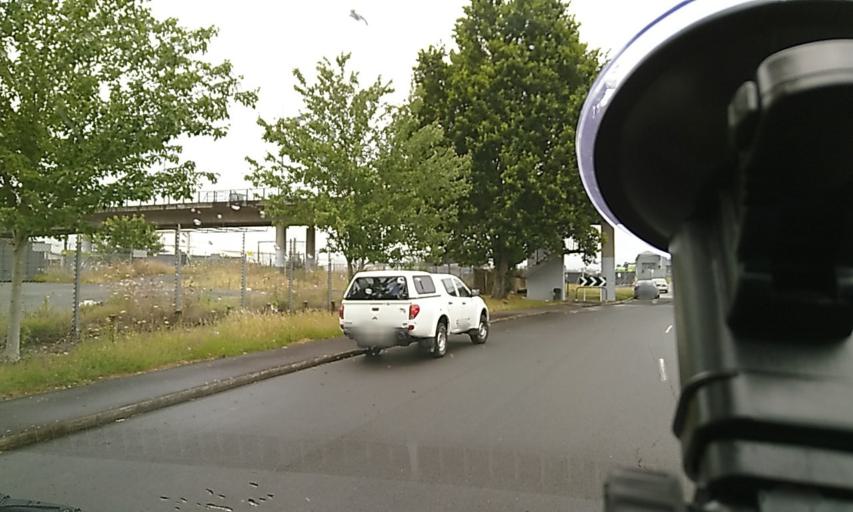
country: NZ
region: Waikato
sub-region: Hamilton City
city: Hamilton
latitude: -37.7881
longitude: 175.2626
